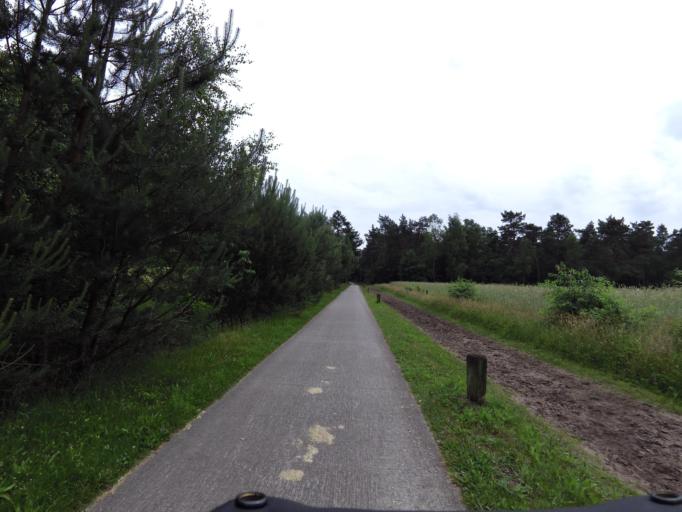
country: NL
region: Gelderland
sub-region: Gemeente Apeldoorn
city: Loenen
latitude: 52.1447
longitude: 6.0151
